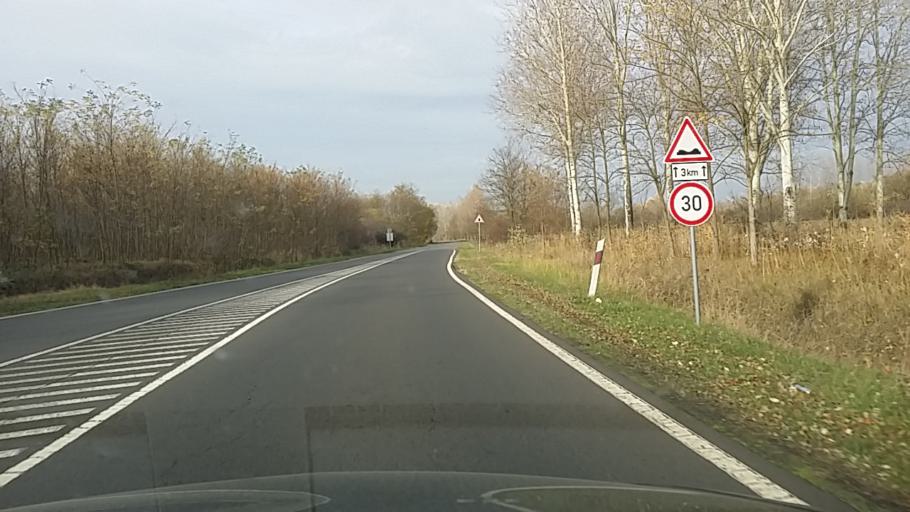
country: HU
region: Szabolcs-Szatmar-Bereg
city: Nyirbogdany
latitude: 48.0439
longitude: 21.8638
